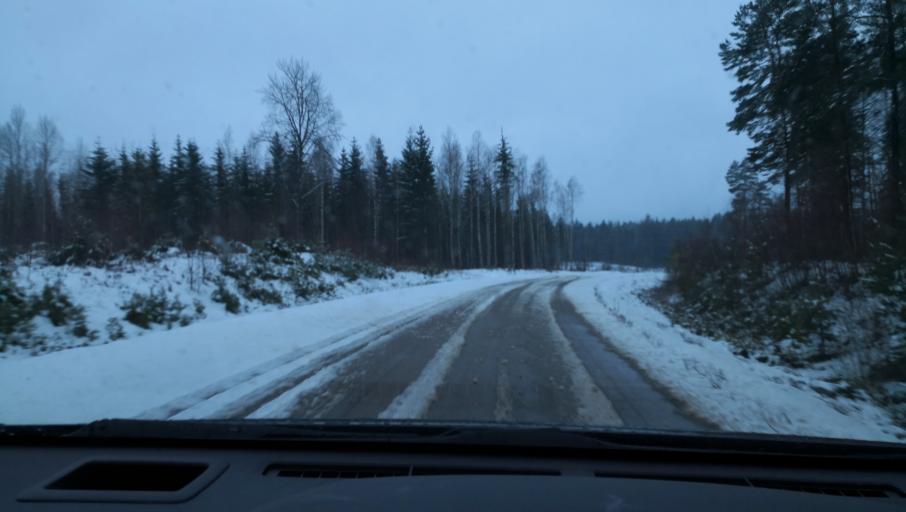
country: SE
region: Vaestmanland
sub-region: Kopings Kommun
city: Koping
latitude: 59.4779
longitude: 15.9645
